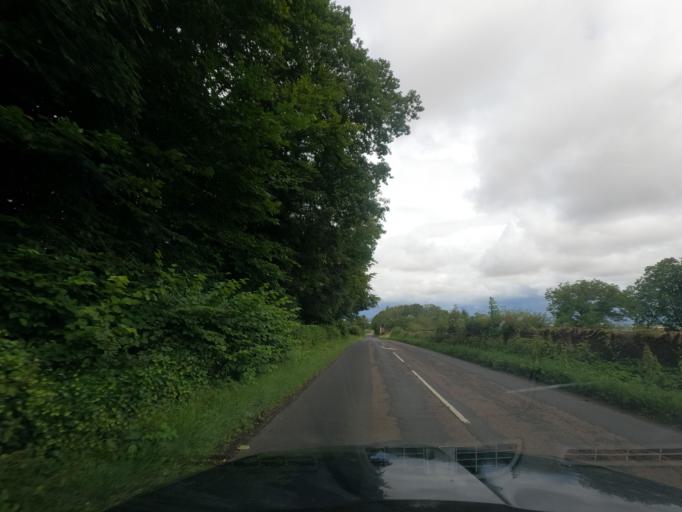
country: GB
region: England
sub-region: Northumberland
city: Lowick
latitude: 55.6539
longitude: -1.9962
